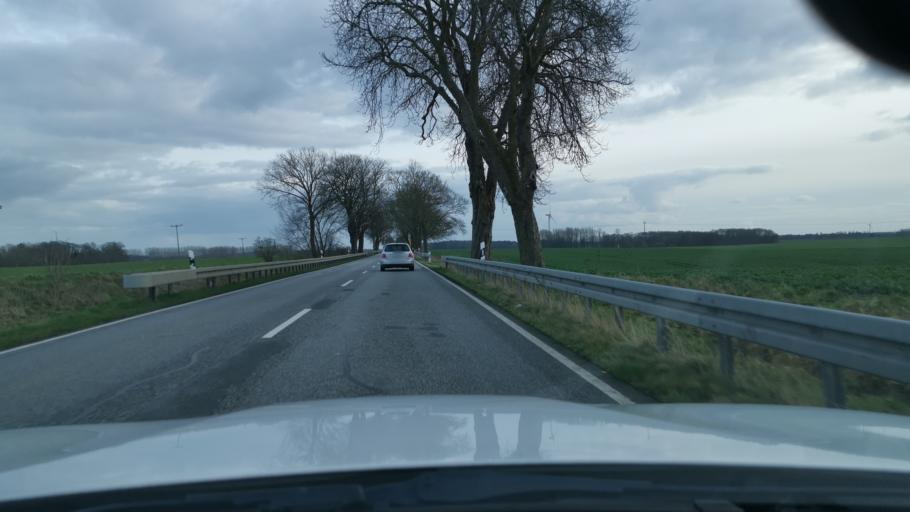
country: DE
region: Mecklenburg-Vorpommern
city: Dummerstorf
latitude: 54.0201
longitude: 12.2439
